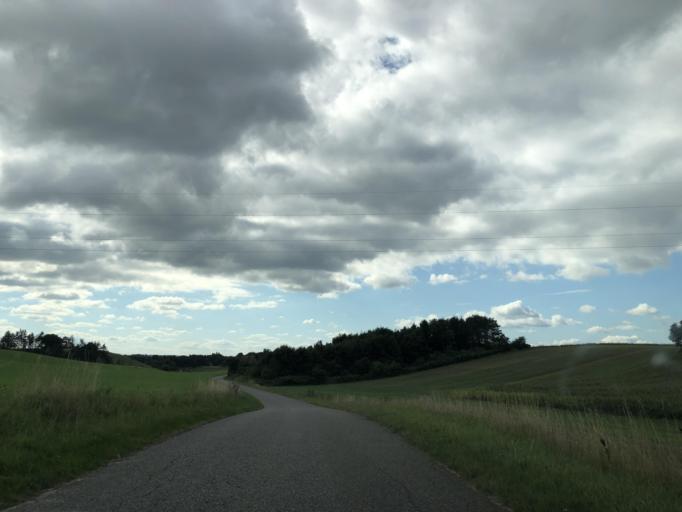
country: DK
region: Central Jutland
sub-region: Viborg Kommune
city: Viborg
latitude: 56.5890
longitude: 9.4014
